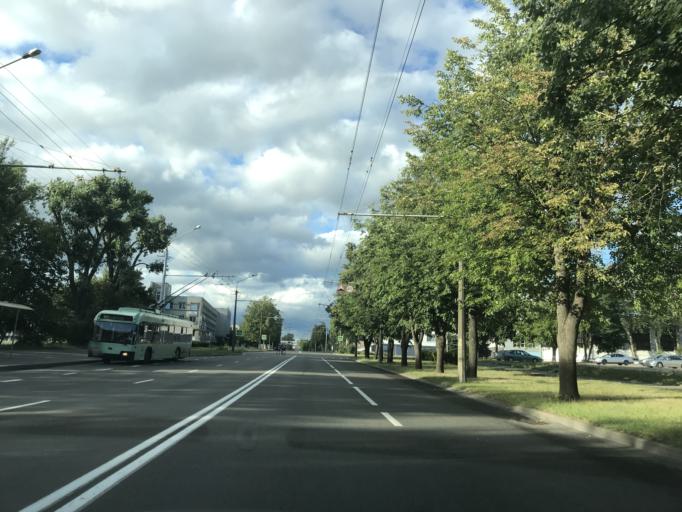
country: BY
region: Minsk
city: Minsk
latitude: 53.9435
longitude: 27.6206
